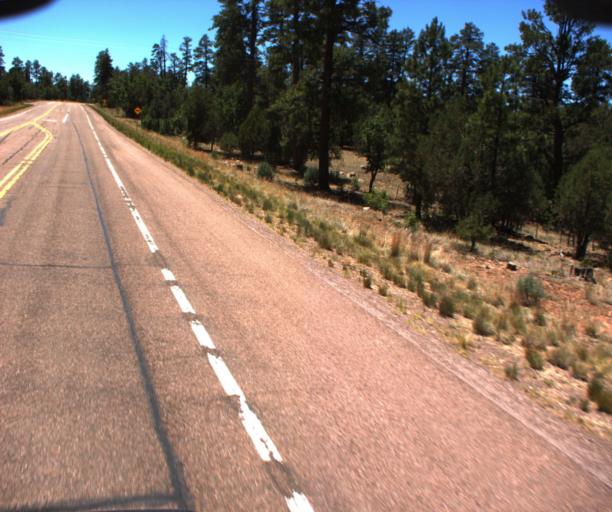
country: US
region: Arizona
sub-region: Gila County
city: Star Valley
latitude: 34.6382
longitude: -111.1106
